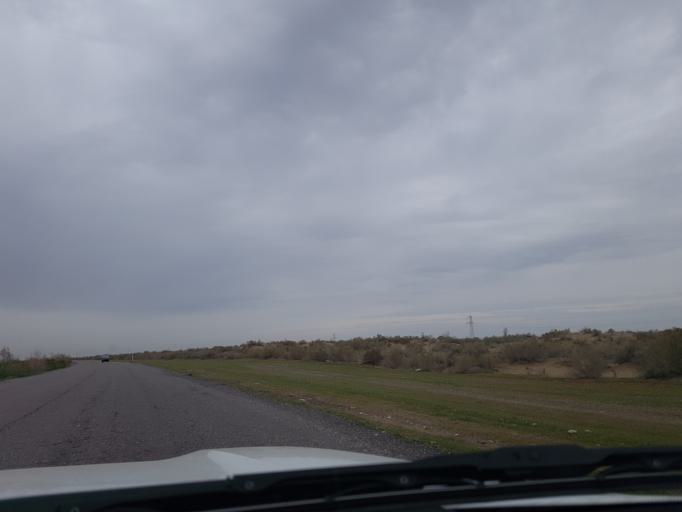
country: TM
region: Lebap
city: Turkmenabat
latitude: 38.8564
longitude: 63.4082
